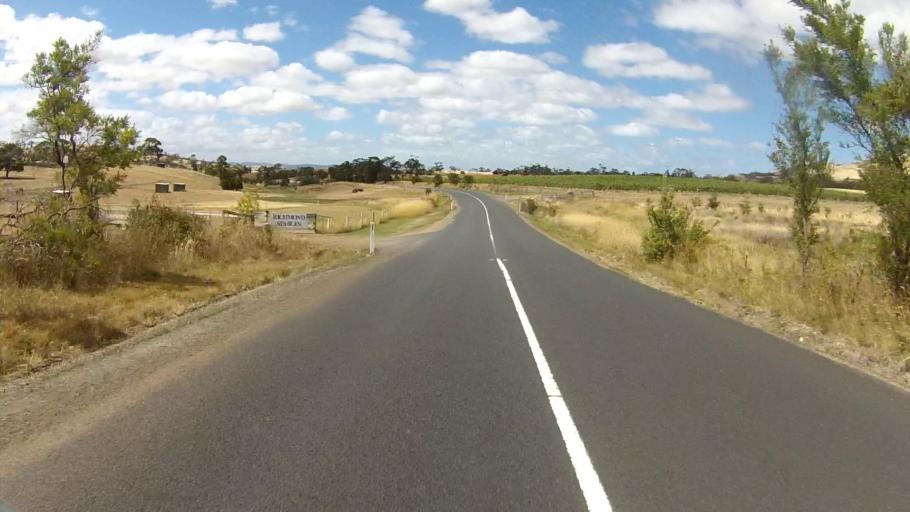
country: AU
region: Tasmania
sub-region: Sorell
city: Sorell
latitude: -42.7489
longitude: 147.4920
